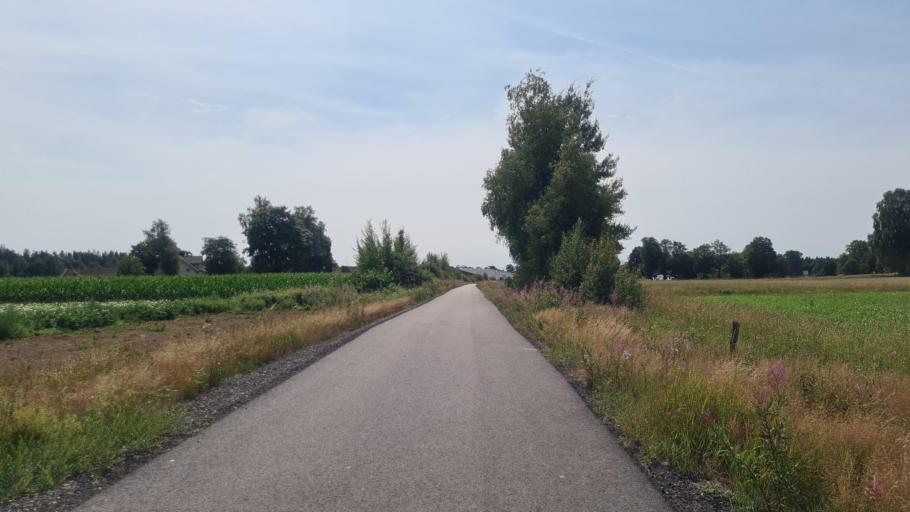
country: SE
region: Kronoberg
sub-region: Ljungby Kommun
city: Lagan
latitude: 56.8765
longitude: 13.9837
